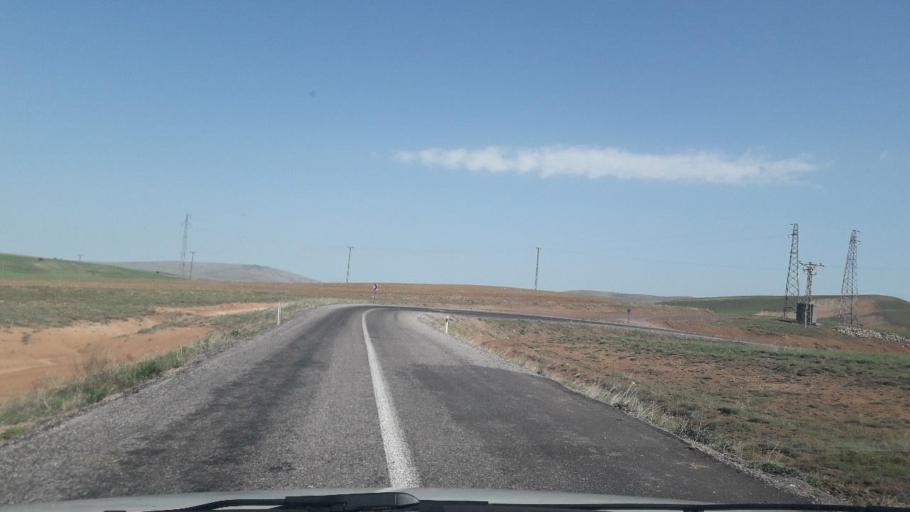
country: TR
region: Sivas
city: Alacahan
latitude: 39.0746
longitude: 37.5464
